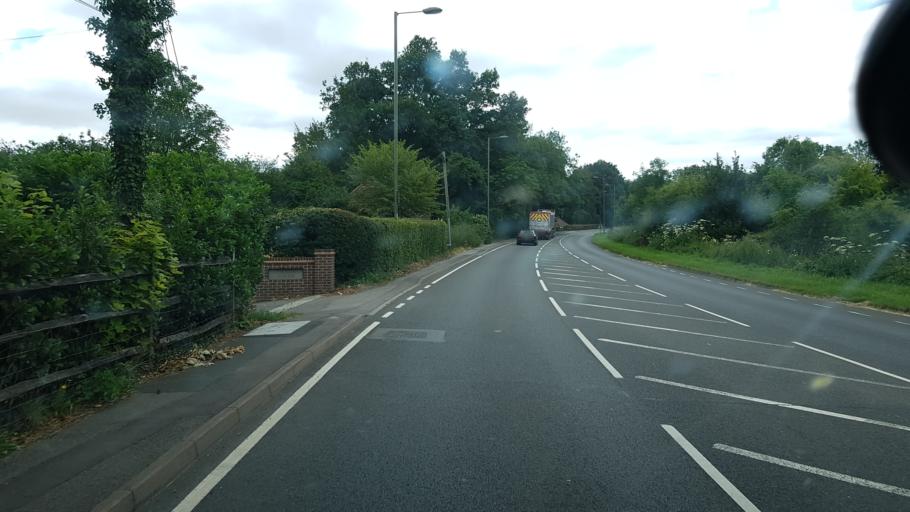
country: GB
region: England
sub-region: Surrey
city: Godstone
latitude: 51.2018
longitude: -0.0554
